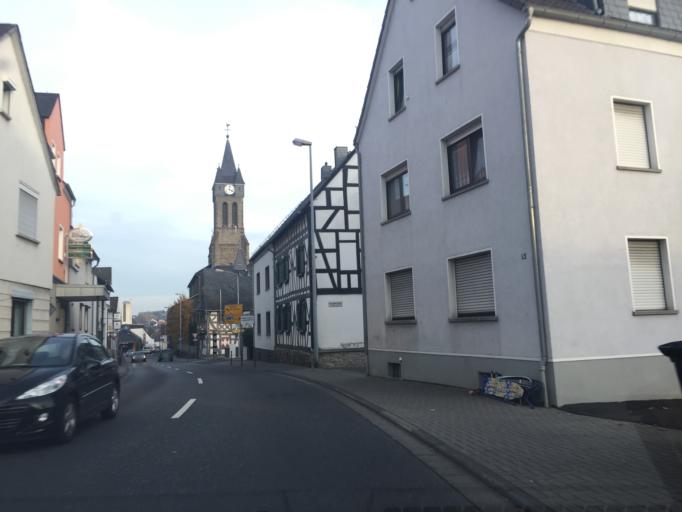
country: DE
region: Hesse
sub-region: Regierungsbezirk Giessen
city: Elz
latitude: 50.4135
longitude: 8.0334
